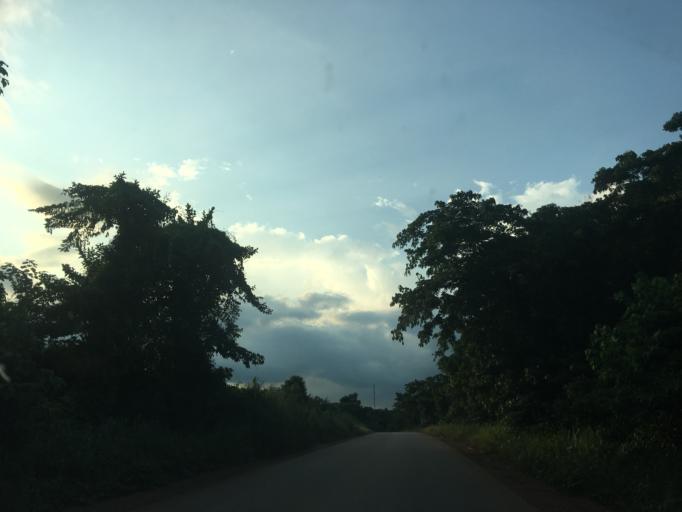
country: GH
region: Western
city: Bibiani
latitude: 6.6751
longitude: -2.4354
